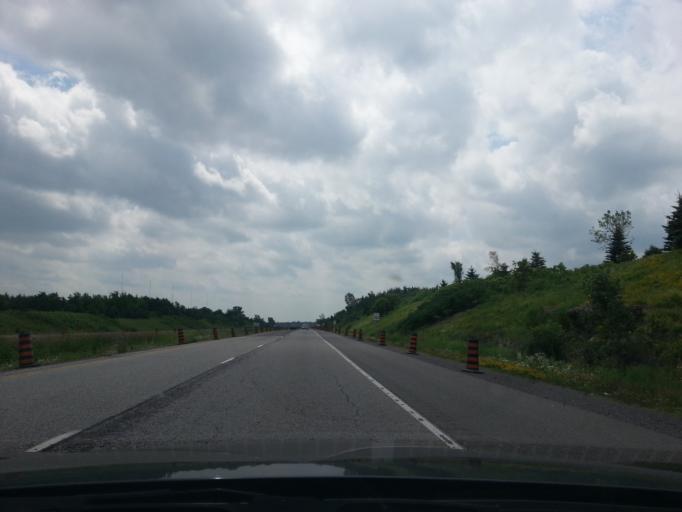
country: CA
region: Ontario
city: Bells Corners
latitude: 45.2633
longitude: -75.7900
